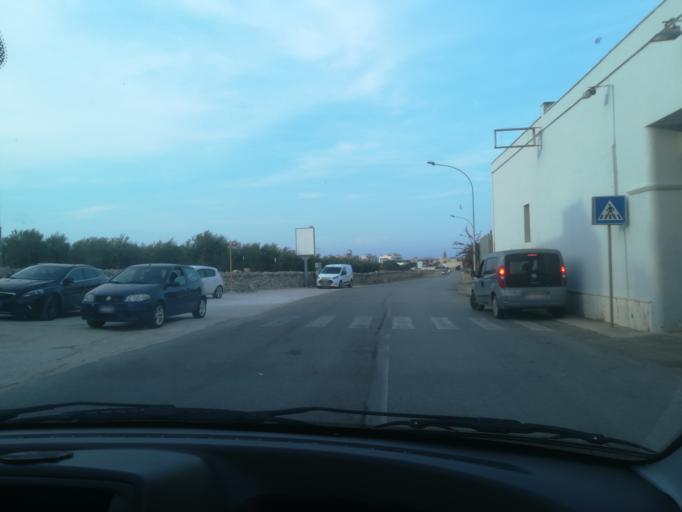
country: IT
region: Apulia
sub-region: Provincia di Bari
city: Monopoli
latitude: 40.9399
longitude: 17.2956
